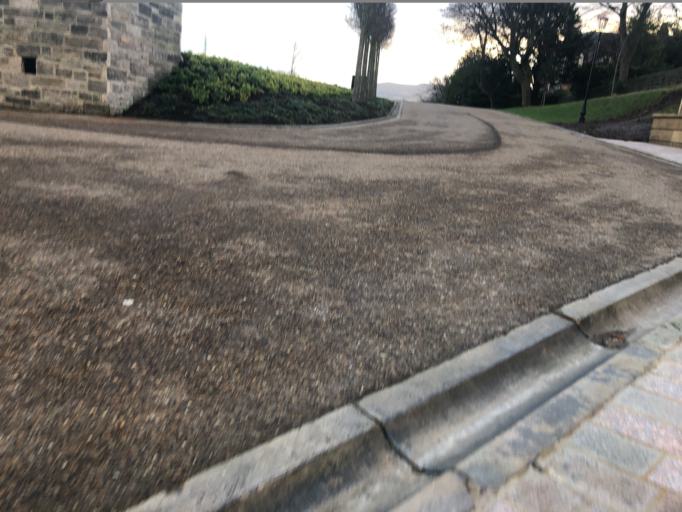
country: GB
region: Scotland
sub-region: Edinburgh
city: Edinburgh
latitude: 55.9475
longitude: -3.2277
